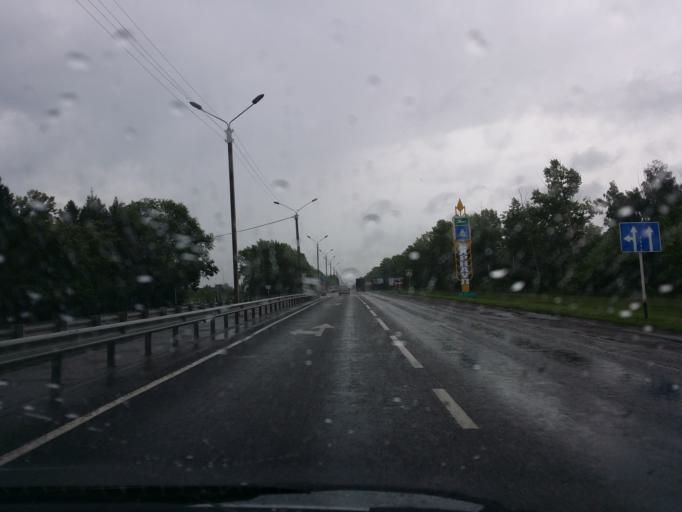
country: RU
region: Altai Krai
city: Vlasikha
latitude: 53.3528
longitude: 83.5657
